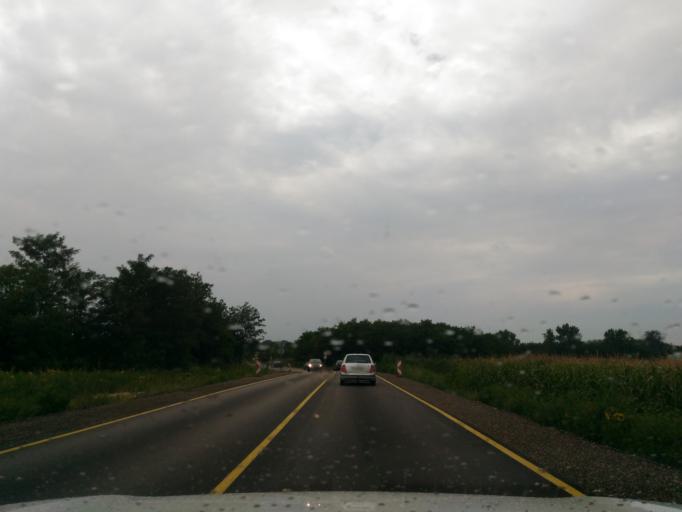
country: HU
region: Pest
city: Albertirsa
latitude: 47.2627
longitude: 19.6128
